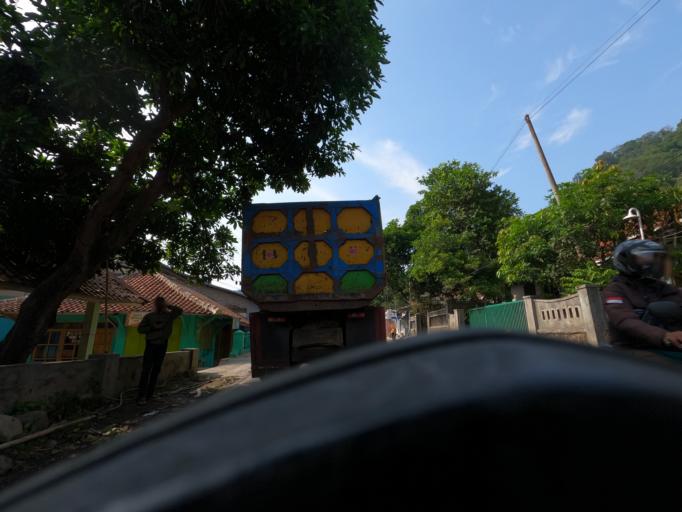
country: ID
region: West Java
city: Lembang
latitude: -6.6391
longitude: 107.7235
